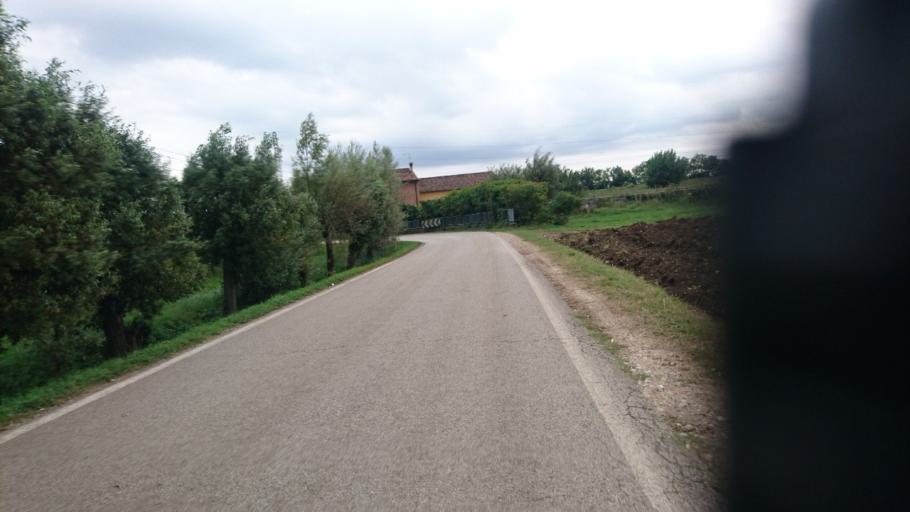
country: IT
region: Veneto
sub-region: Provincia di Vicenza
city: Gambellara
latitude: 45.4354
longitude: 11.3433
